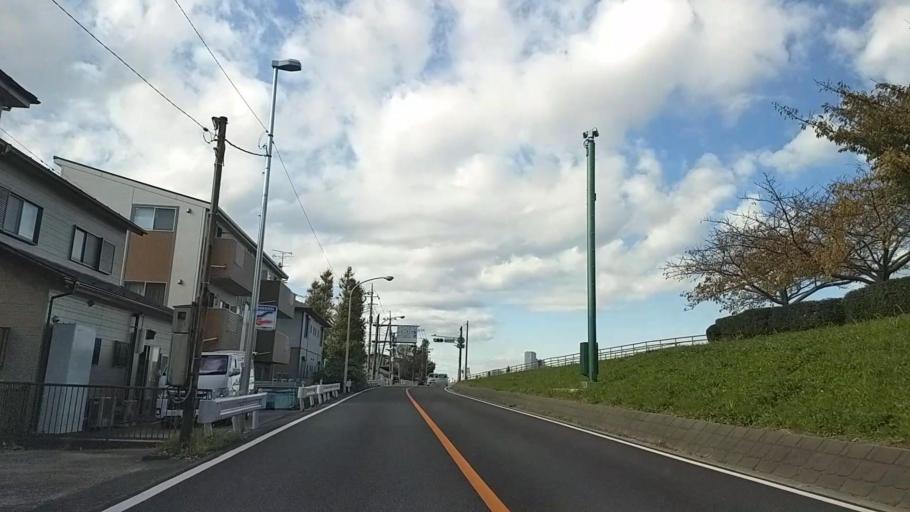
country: JP
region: Kanagawa
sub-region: Kawasaki-shi
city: Kawasaki
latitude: 35.5900
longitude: 139.6516
